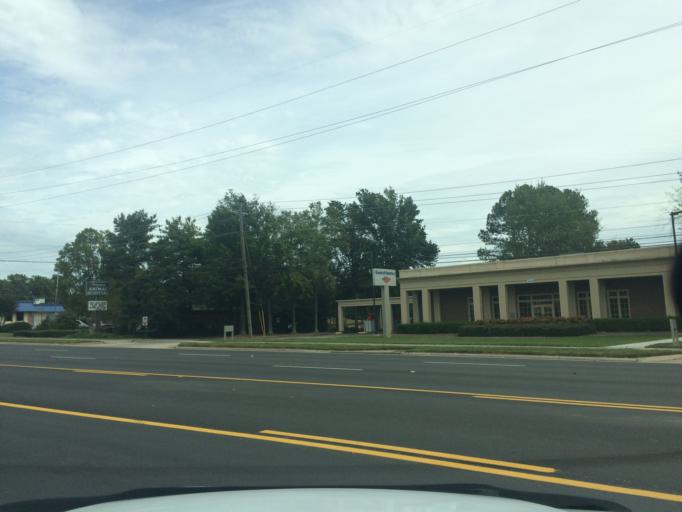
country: US
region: Georgia
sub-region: Cobb County
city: Fair Oaks
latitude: 33.8926
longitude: -84.5380
